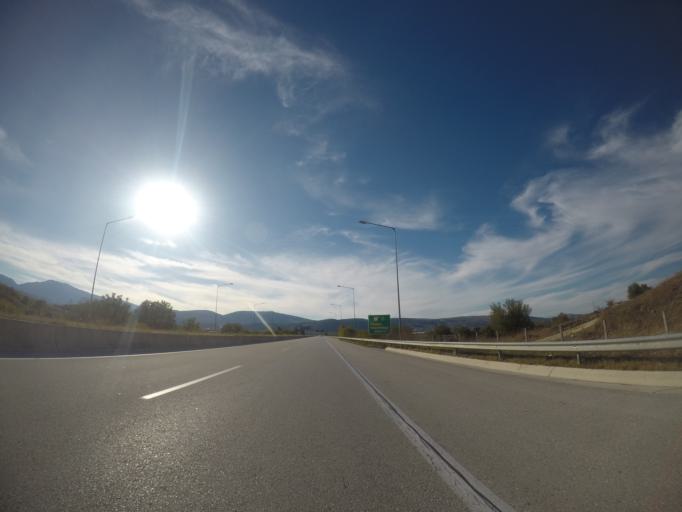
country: GR
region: Epirus
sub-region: Nomos Ioanninon
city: Katsikas
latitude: 39.6033
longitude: 20.8846
